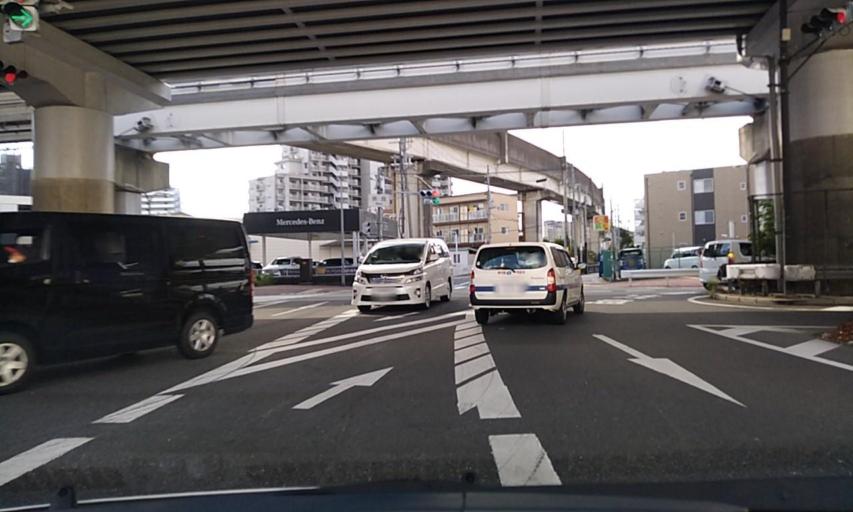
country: JP
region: Osaka
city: Ibaraki
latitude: 34.8058
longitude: 135.5633
